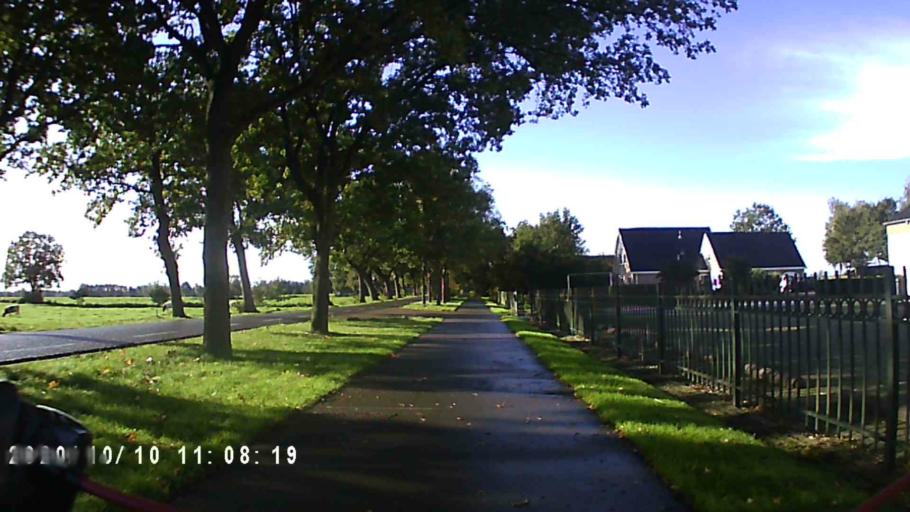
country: NL
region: Friesland
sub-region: Gemeente Smallingerland
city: Drachtstercompagnie
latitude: 53.1213
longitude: 6.2114
